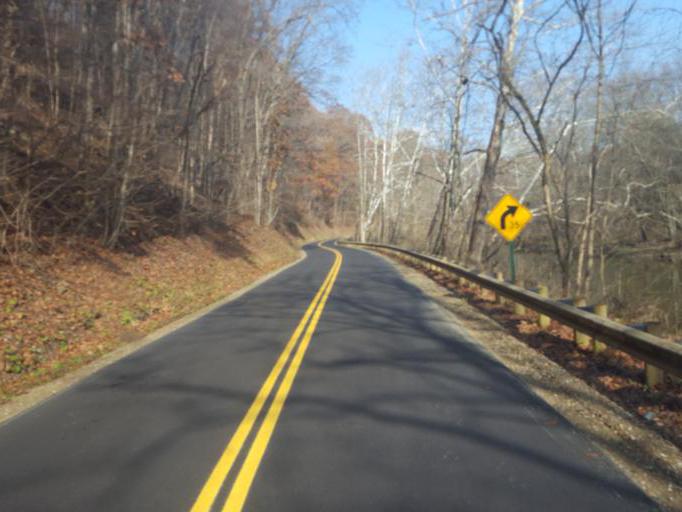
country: US
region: Ohio
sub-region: Ashland County
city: Loudonville
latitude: 40.5640
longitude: -82.1997
